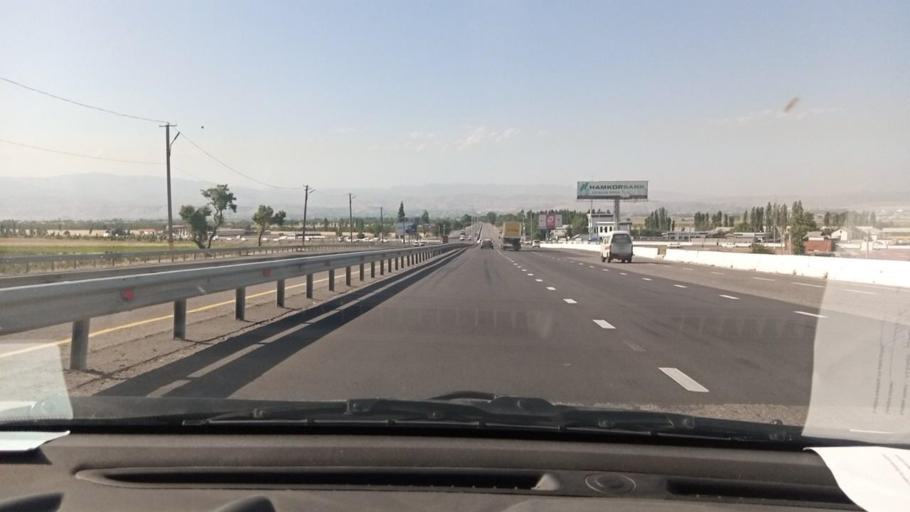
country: UZ
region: Toshkent
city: Ohangaron
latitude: 40.9232
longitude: 69.5969
